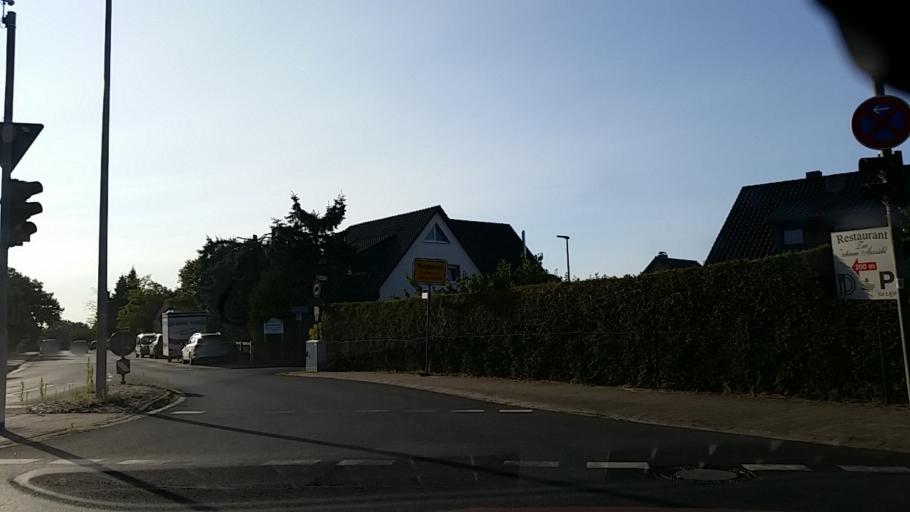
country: DE
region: Lower Saxony
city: Lehre
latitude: 52.3163
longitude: 10.6400
